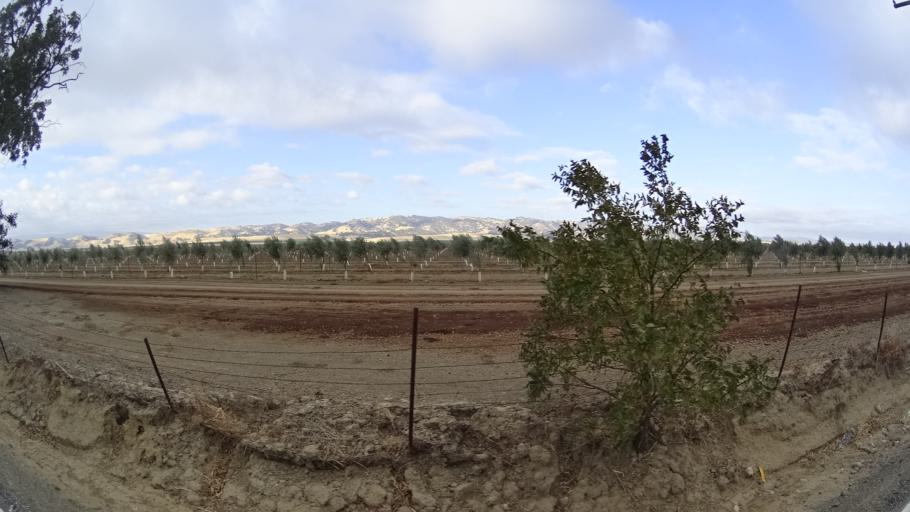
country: US
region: California
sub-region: Yolo County
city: Esparto
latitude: 38.7854
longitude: -122.0437
